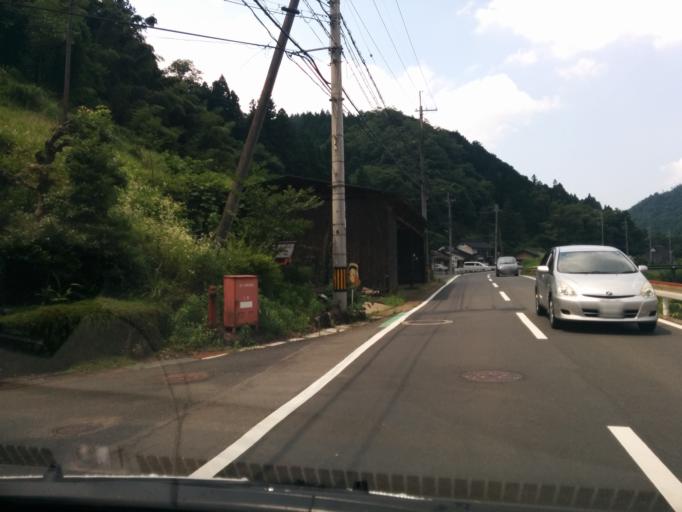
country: JP
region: Kyoto
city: Miyazu
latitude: 35.4174
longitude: 135.1543
